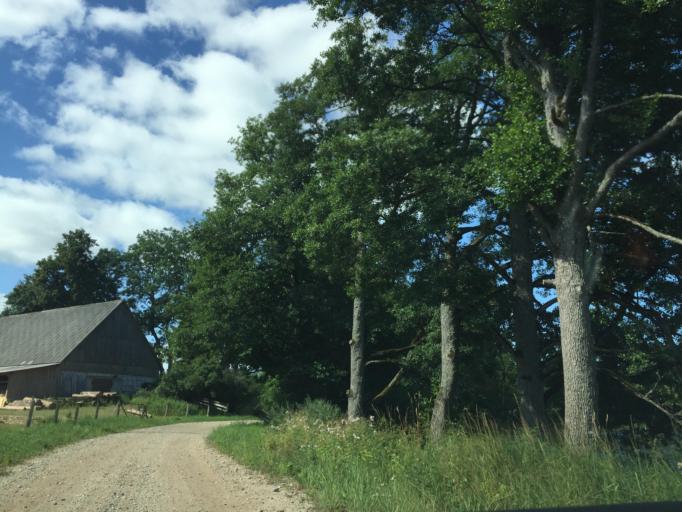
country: LV
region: Talsu Rajons
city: Stende
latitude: 57.1542
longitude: 22.2985
